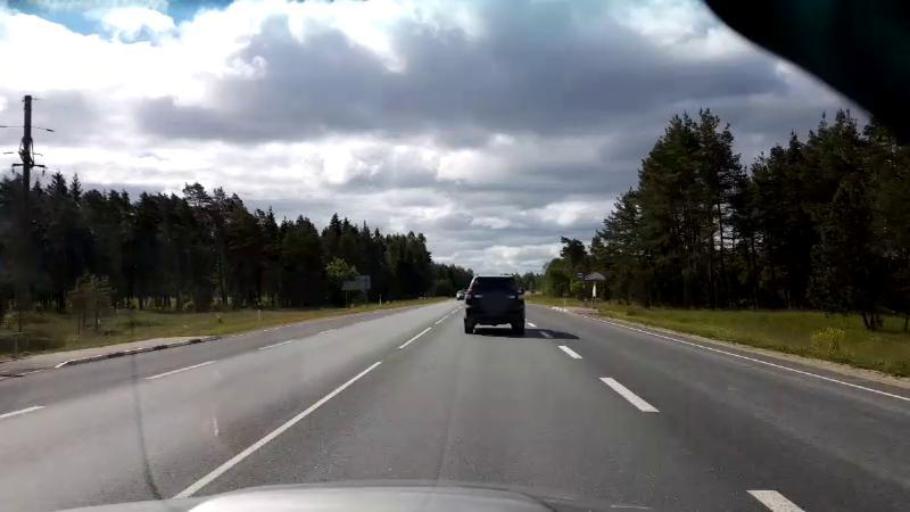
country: EE
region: Raplamaa
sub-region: Maerjamaa vald
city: Marjamaa
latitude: 58.9744
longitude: 24.4755
